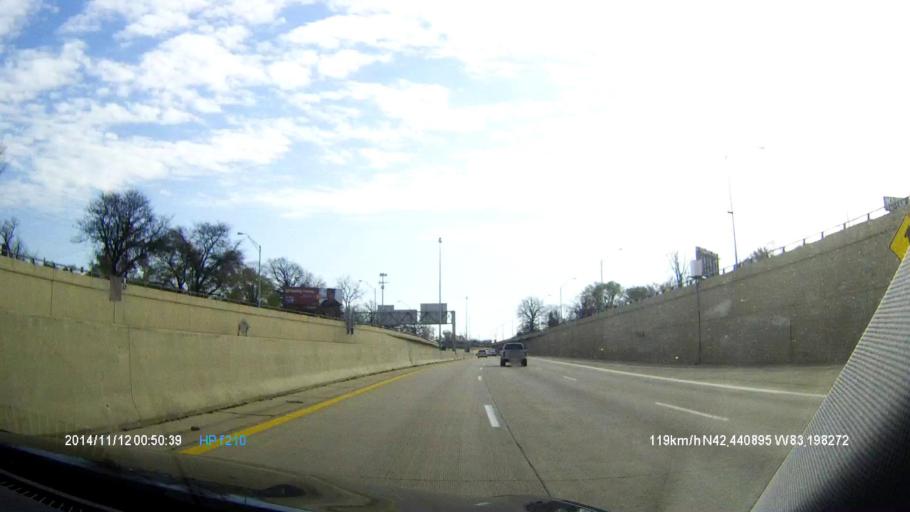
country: US
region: Michigan
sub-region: Oakland County
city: Oak Park
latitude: 42.4405
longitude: -83.1978
